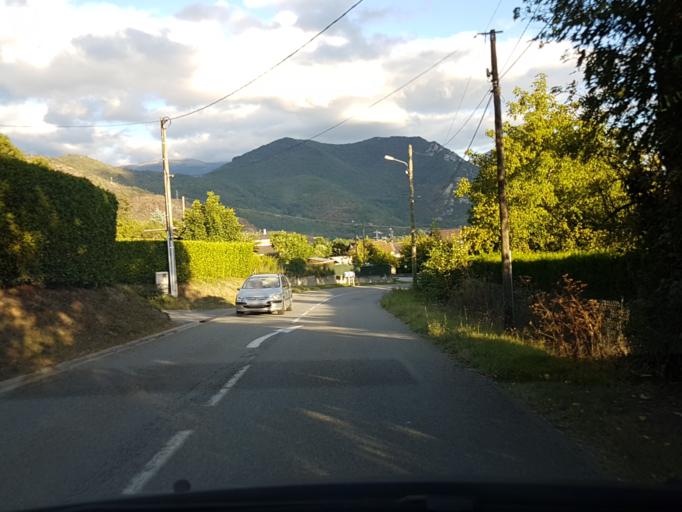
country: FR
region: Midi-Pyrenees
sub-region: Departement de l'Ariege
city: Tarascon-sur-Ariege
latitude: 42.8579
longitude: 1.5821
